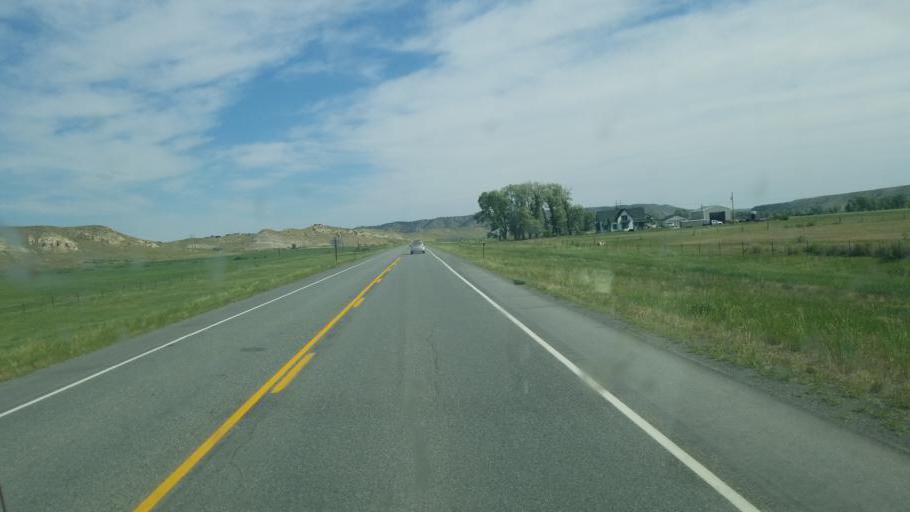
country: US
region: Wyoming
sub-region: Park County
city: Cody
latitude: 44.1646
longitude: -108.8761
